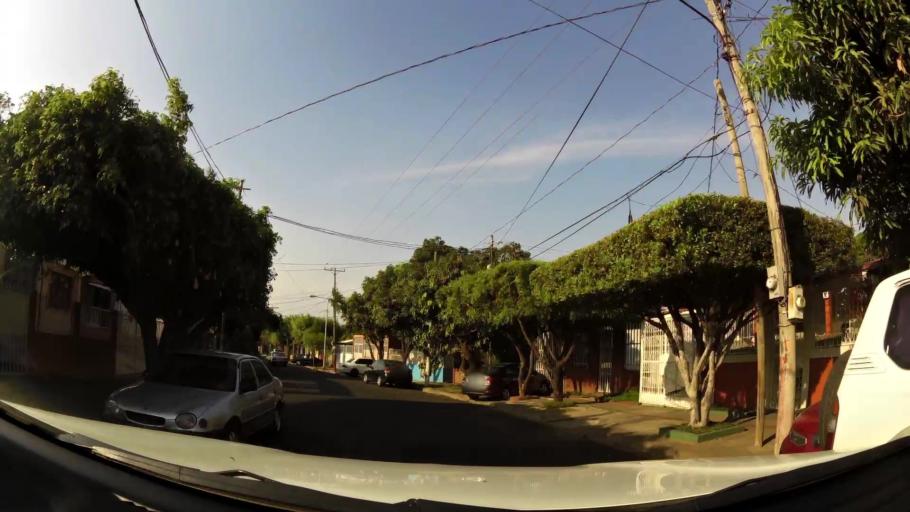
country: NI
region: Managua
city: Managua
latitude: 12.1203
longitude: -86.2487
